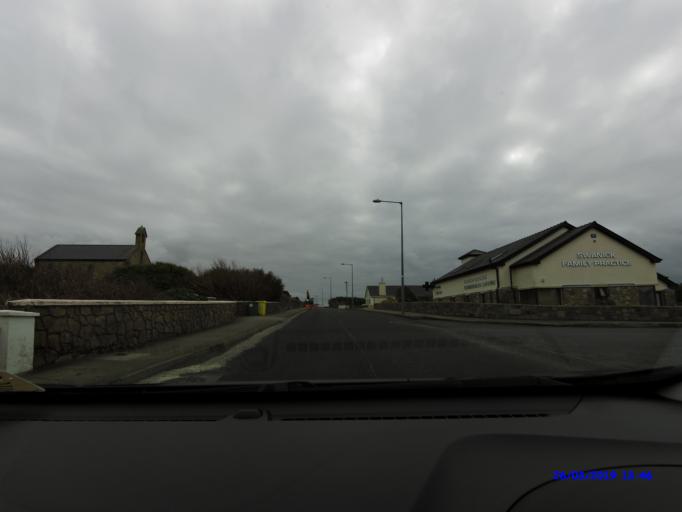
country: IE
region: Connaught
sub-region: Maigh Eo
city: Belmullet
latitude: 54.2209
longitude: -9.9865
